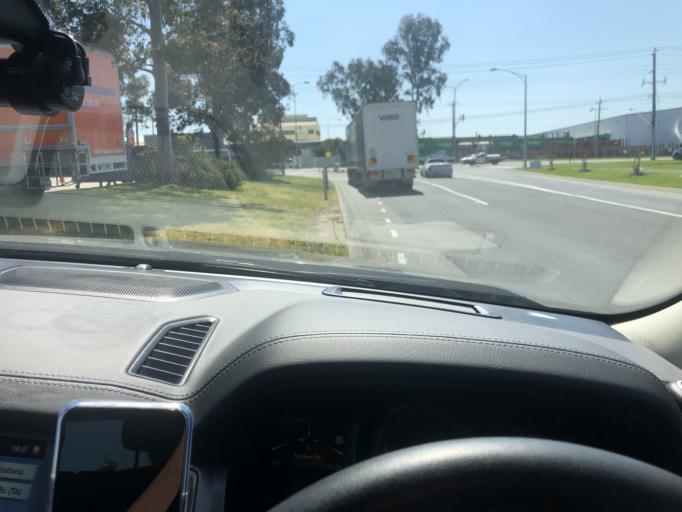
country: AU
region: Victoria
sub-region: Casey
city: Doveton
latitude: -38.0166
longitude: 145.2256
